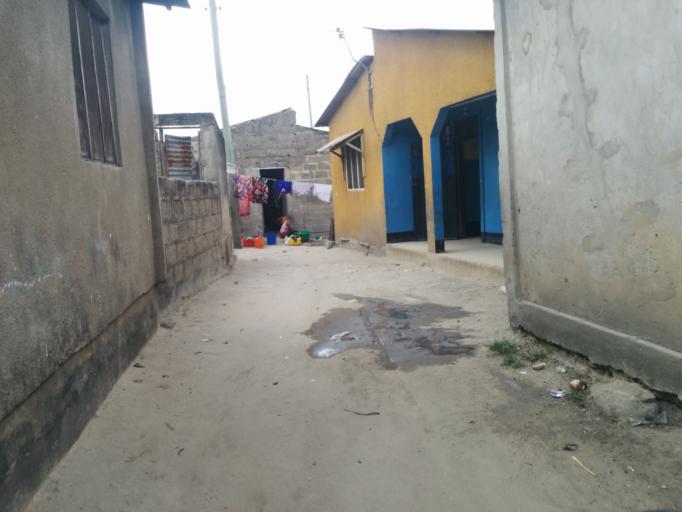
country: TZ
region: Dar es Salaam
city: Dar es Salaam
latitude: -6.8592
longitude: 39.2452
